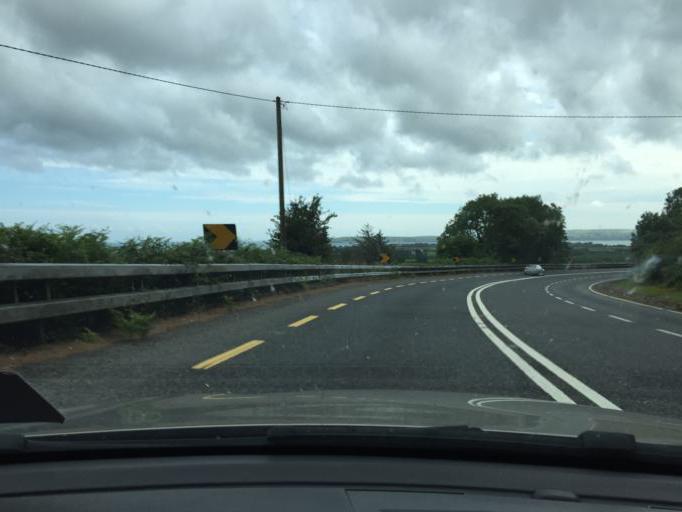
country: IE
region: Munster
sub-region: Waterford
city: Dungarvan
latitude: 52.1161
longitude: -7.5564
